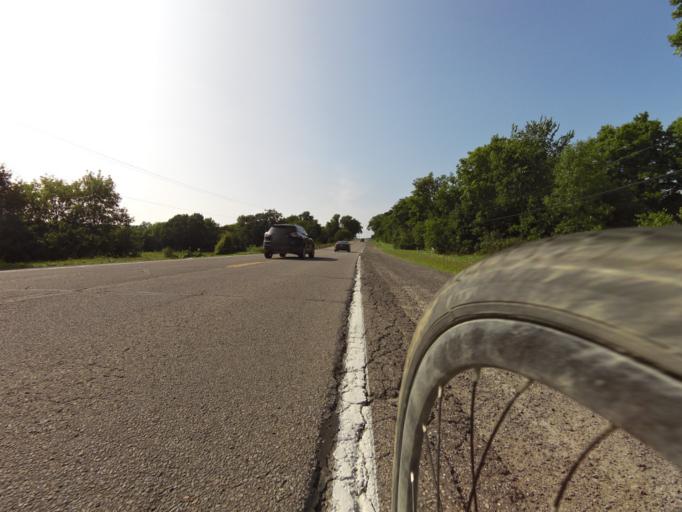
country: CA
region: Ontario
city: Kingston
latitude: 44.3534
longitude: -76.6445
